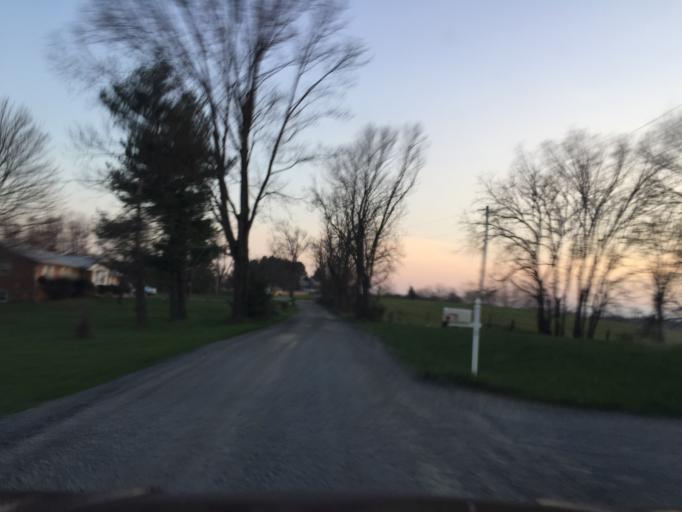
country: US
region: Maryland
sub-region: Frederick County
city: Brunswick
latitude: 39.2885
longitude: -77.5969
